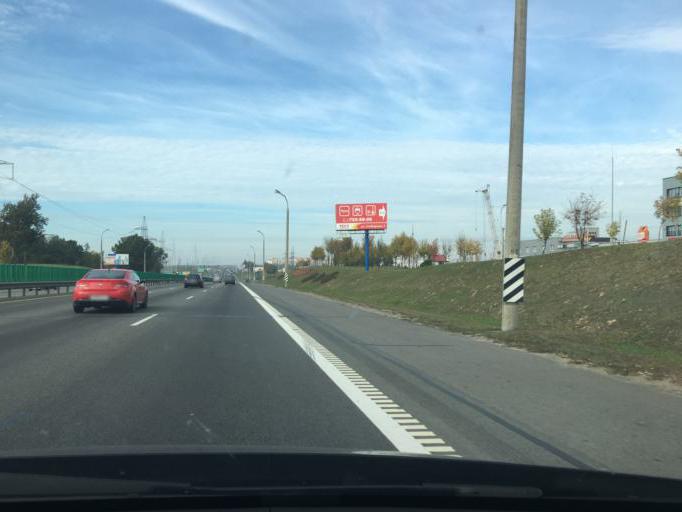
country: BY
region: Minsk
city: Malinovka
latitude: 53.8639
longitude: 27.4258
